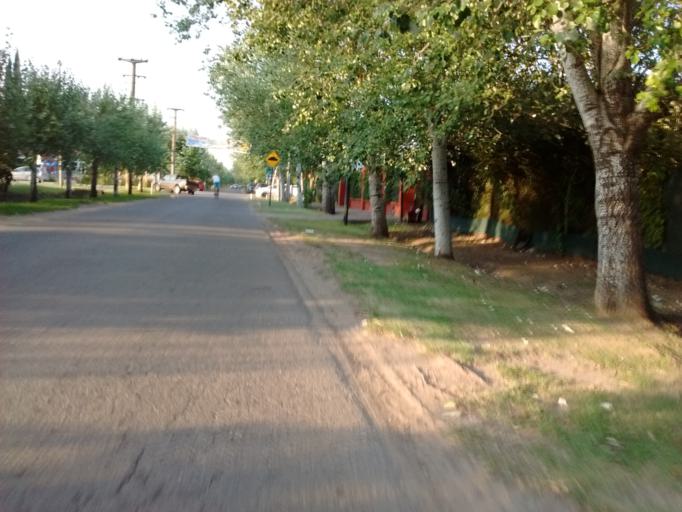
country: AR
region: Santa Fe
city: Funes
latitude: -32.9179
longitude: -60.7598
